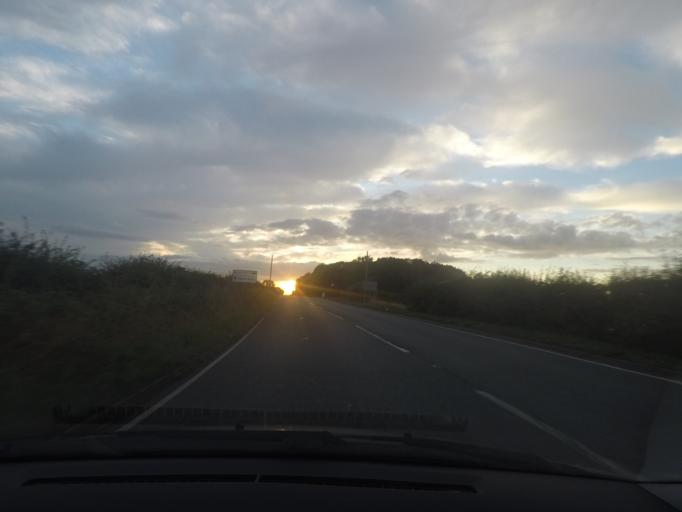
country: GB
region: England
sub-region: North Lincolnshire
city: Croxton
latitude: 53.5827
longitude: -0.3253
